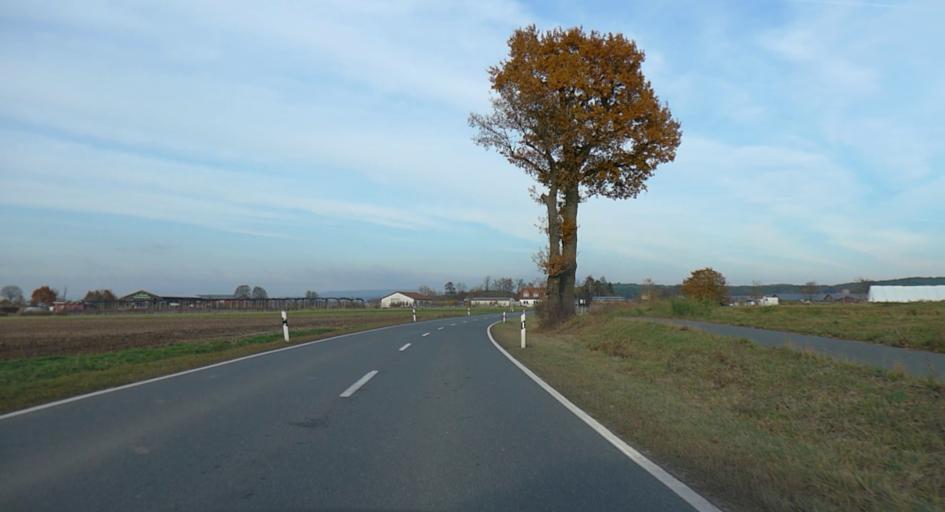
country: DE
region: Bavaria
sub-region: Upper Franconia
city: Poxdorf
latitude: 49.6616
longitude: 11.0605
